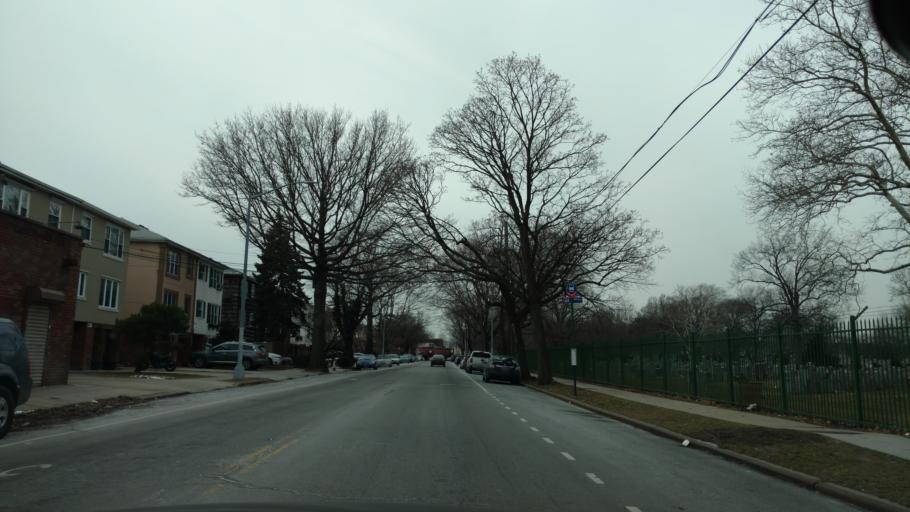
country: US
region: New York
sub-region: Queens County
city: Borough of Queens
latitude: 40.7121
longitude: -73.8624
